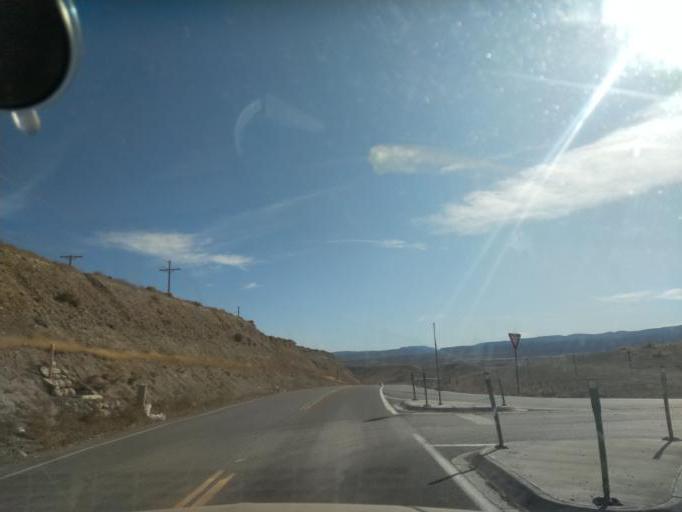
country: US
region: Colorado
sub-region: Mesa County
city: Fruitvale
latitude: 39.0146
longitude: -108.4841
